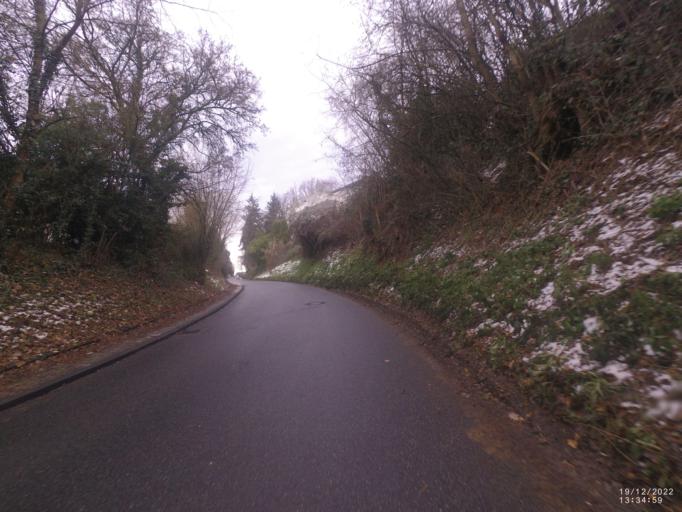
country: DE
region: Rheinland-Pfalz
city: Unkel
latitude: 50.6114
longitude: 7.2044
